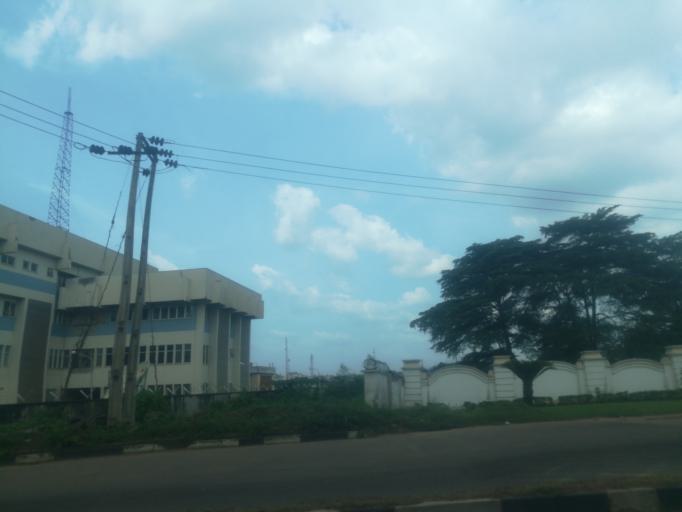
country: NG
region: Ogun
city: Abeokuta
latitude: 7.1381
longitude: 3.3422
